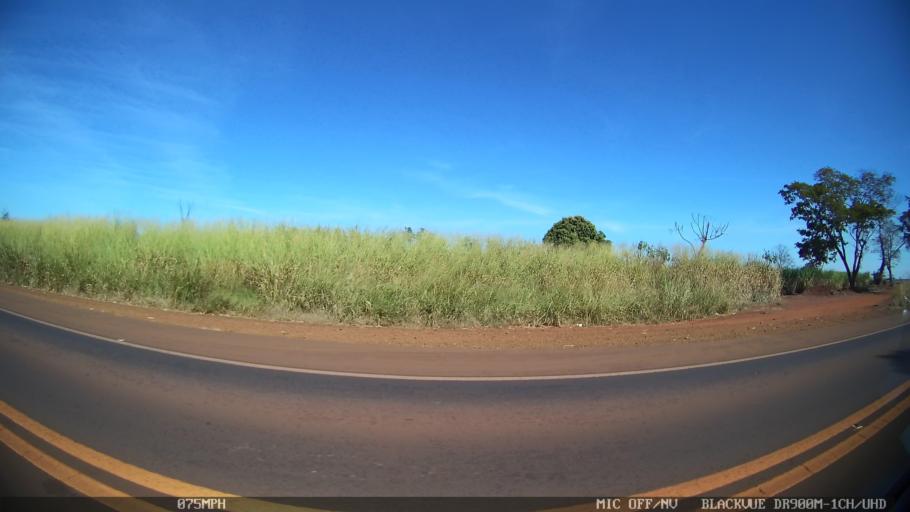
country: BR
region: Sao Paulo
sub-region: Sao Joaquim Da Barra
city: Sao Joaquim da Barra
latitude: -20.5396
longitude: -47.8164
